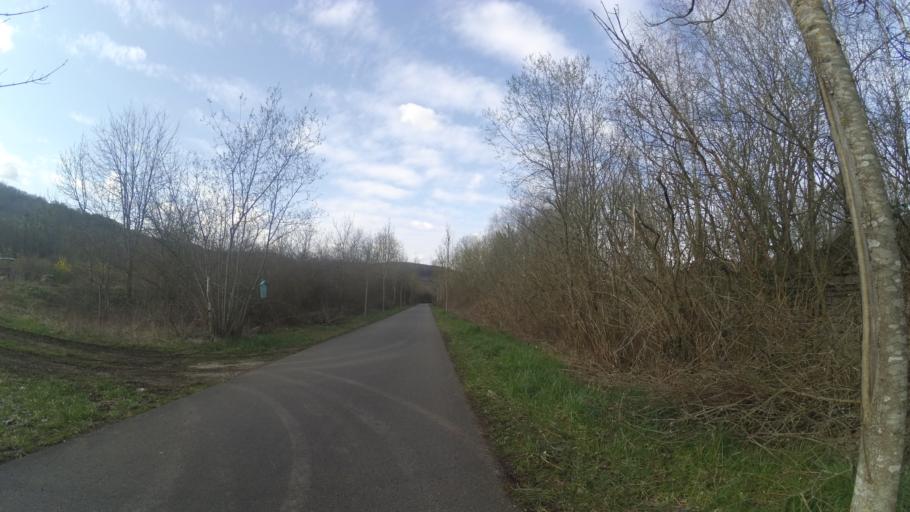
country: DE
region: Saarland
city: Gersheim
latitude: 49.1523
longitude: 7.2084
